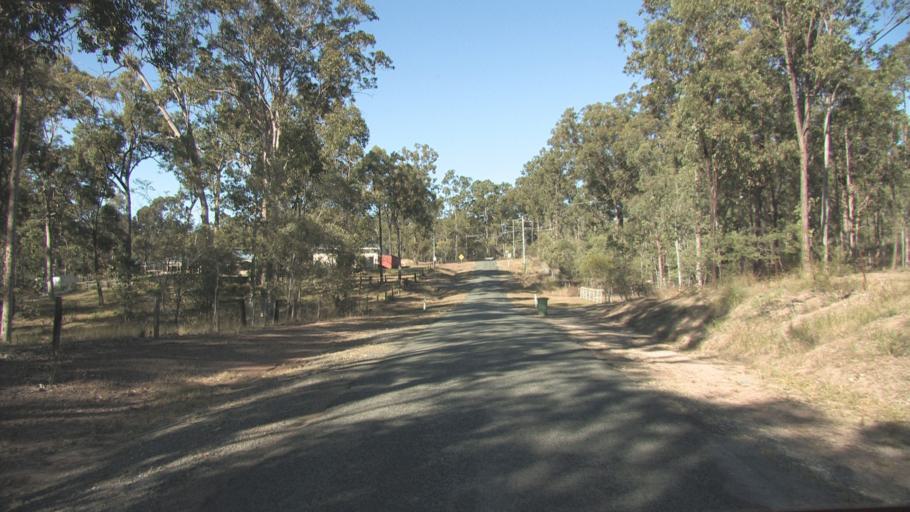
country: AU
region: Queensland
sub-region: Ipswich
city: Springfield Lakes
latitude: -27.6914
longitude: 152.9296
